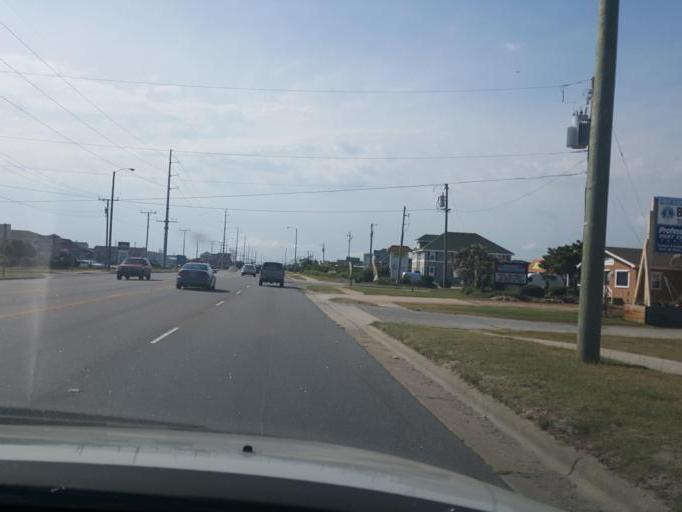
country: US
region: North Carolina
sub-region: Dare County
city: Kill Devil Hills
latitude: 36.0466
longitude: -75.6810
